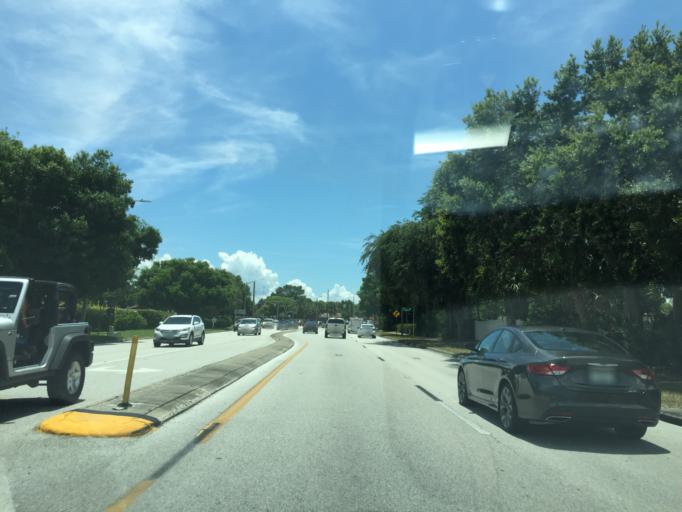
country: US
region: Florida
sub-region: Pinellas County
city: Dunedin
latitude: 28.0096
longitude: -82.7447
